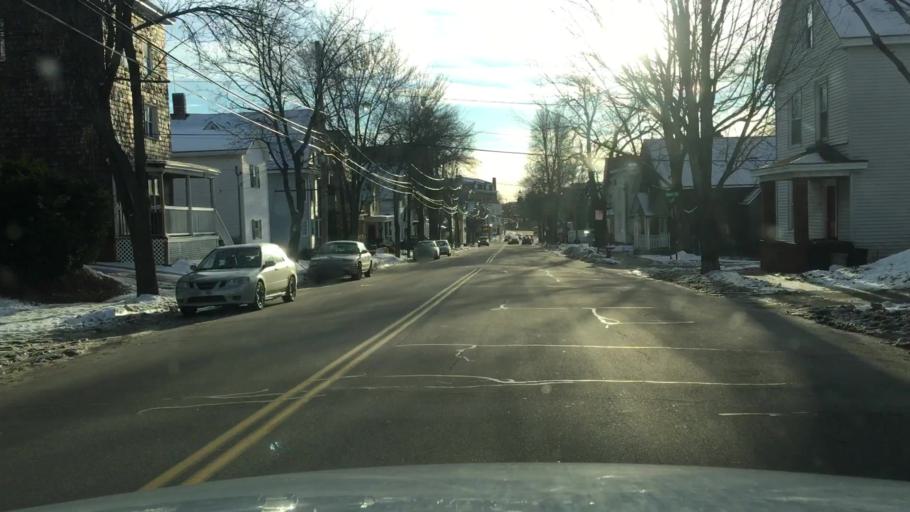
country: US
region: Maine
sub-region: Androscoggin County
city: Lewiston
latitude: 44.1018
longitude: -70.2105
